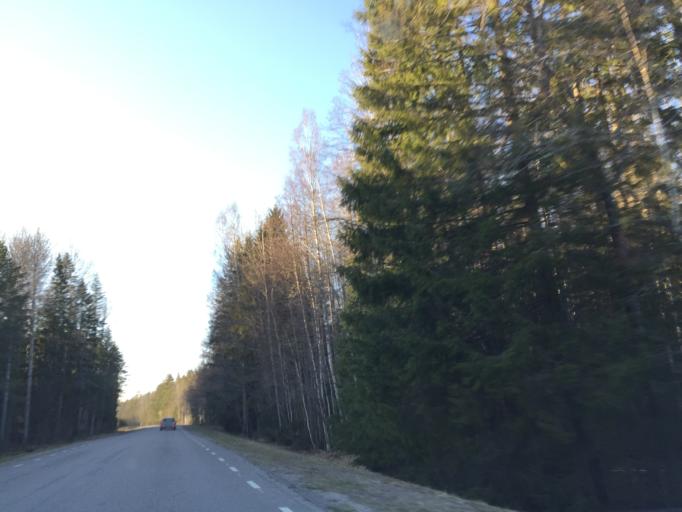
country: EE
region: Ida-Virumaa
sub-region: Toila vald
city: Voka
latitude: 59.1522
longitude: 27.6065
